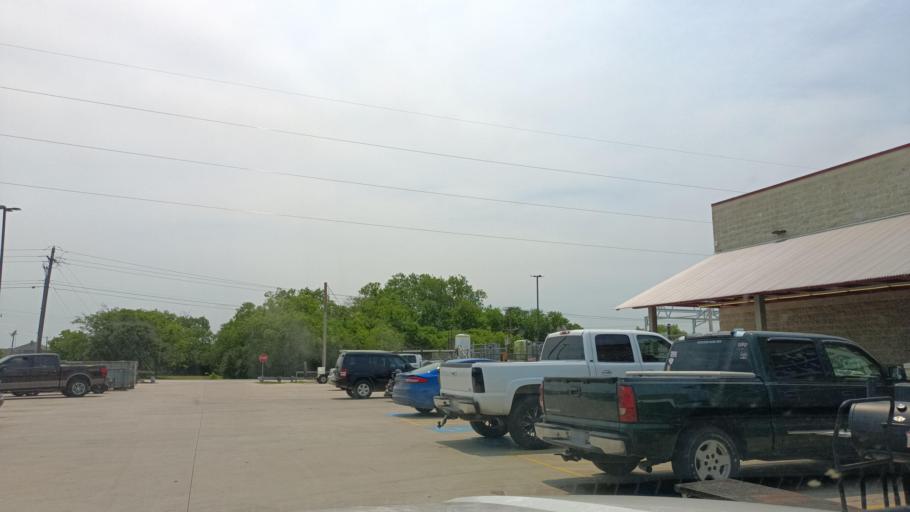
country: US
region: Texas
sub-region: Bell County
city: Temple
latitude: 31.0604
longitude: -97.3384
